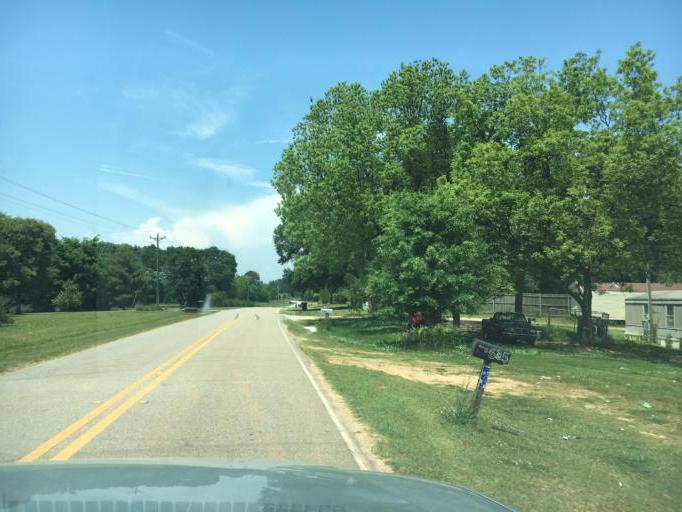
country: US
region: Georgia
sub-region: Hart County
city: Royston
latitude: 34.3012
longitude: -83.0919
